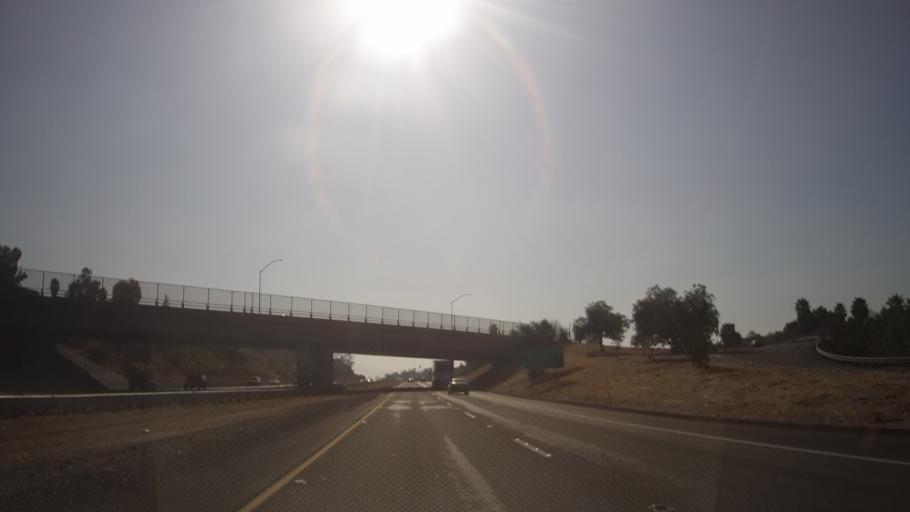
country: US
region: California
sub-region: San Diego County
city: Casa de Oro-Mount Helix
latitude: 32.7438
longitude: -116.9754
